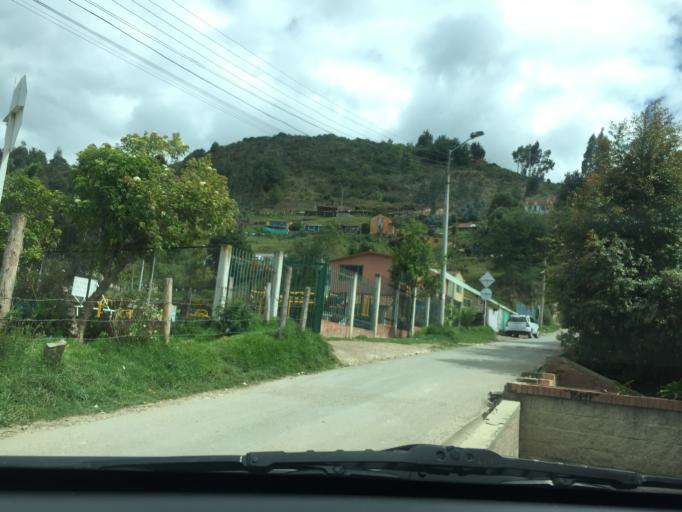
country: CO
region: Cundinamarca
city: Tocancipa
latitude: 4.9683
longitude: -73.8996
